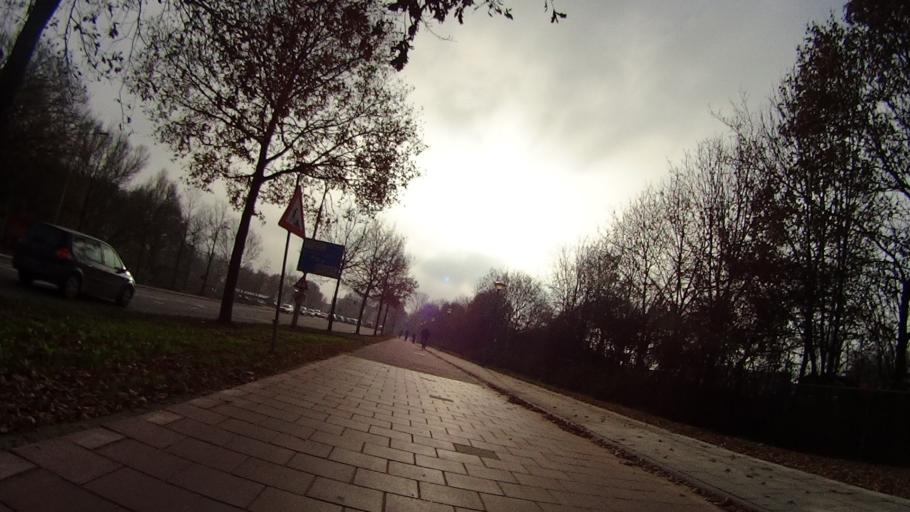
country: NL
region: Utrecht
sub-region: Gemeente Amersfoort
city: Hoogland
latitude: 52.1678
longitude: 5.3754
